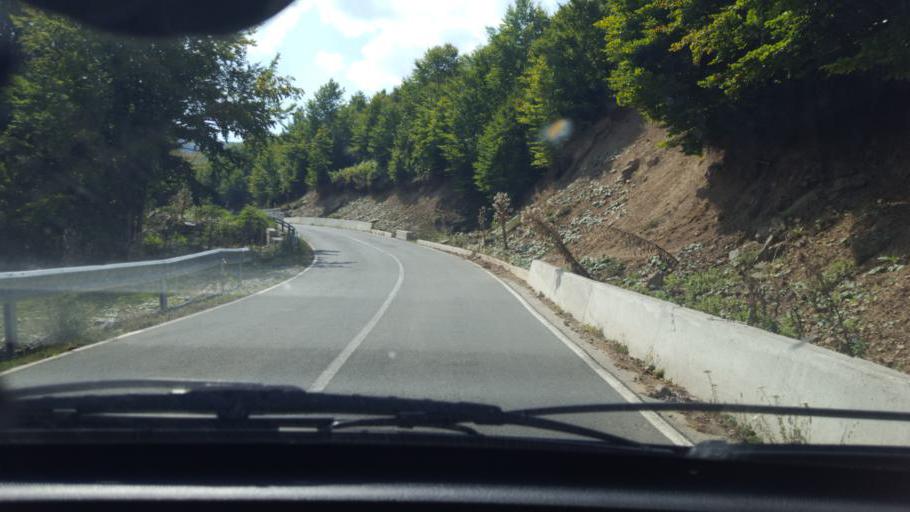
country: AL
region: Kukes
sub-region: Rrethi i Tropojes
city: Valbone
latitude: 42.5447
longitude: 19.7203
